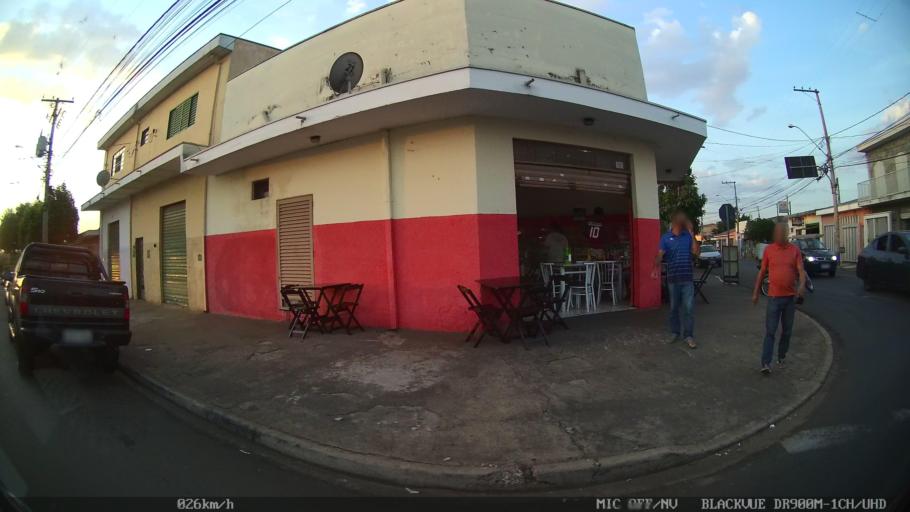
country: BR
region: Sao Paulo
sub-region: Ribeirao Preto
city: Ribeirao Preto
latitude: -21.1393
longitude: -47.8214
